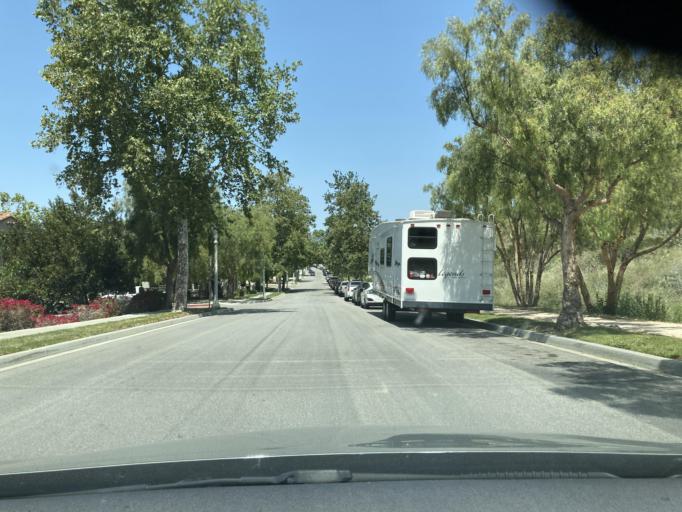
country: US
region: California
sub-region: Ventura County
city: Camarillo
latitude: 34.1659
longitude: -119.0339
